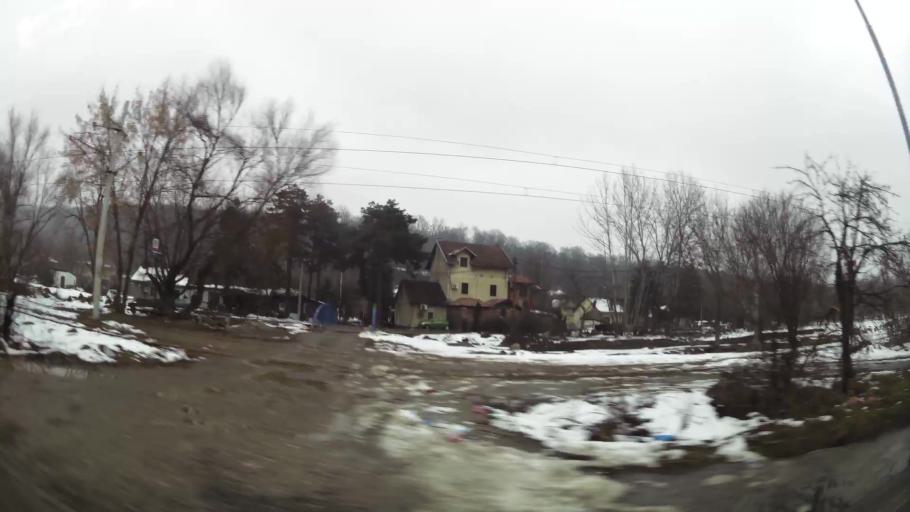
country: RS
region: Central Serbia
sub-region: Belgrade
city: Rakovica
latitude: 44.7606
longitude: 20.4454
